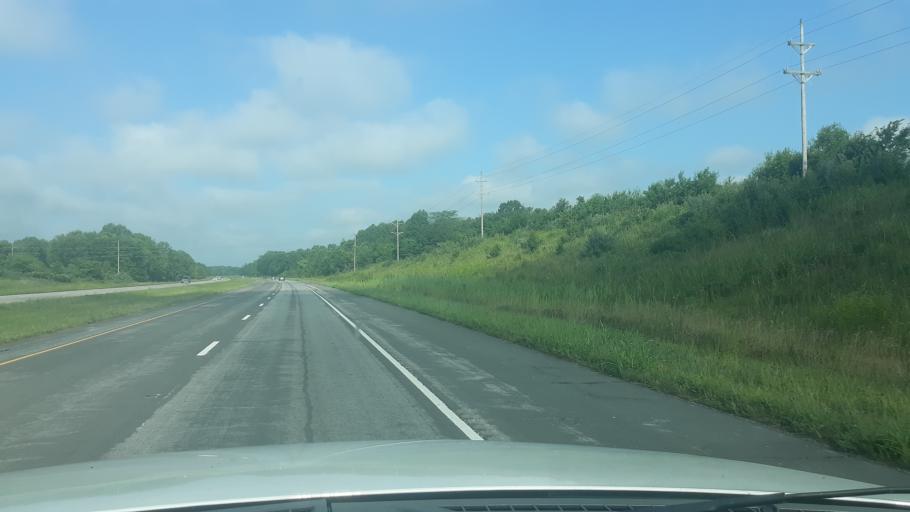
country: US
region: Illinois
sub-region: Saline County
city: Carrier Mills
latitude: 37.7339
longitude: -88.6773
